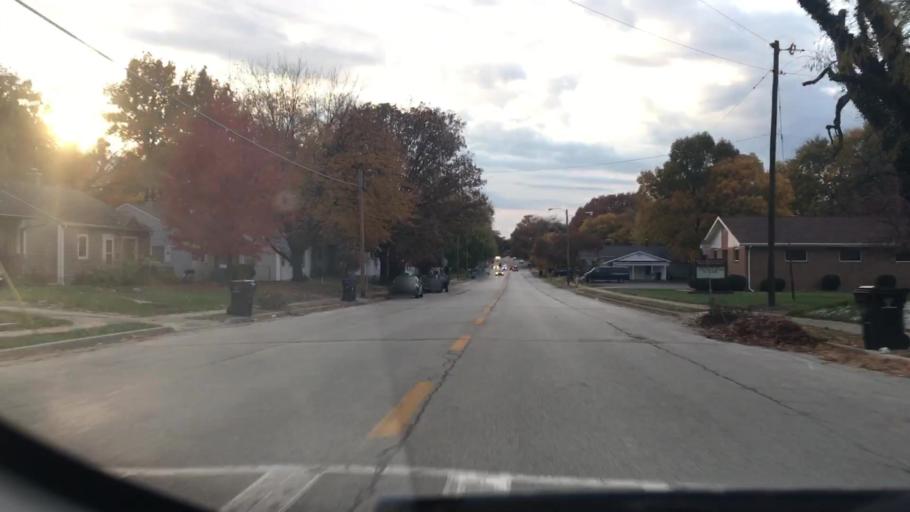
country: US
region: Illinois
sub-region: McLean County
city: Bloomington
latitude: 40.4933
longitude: -88.9780
